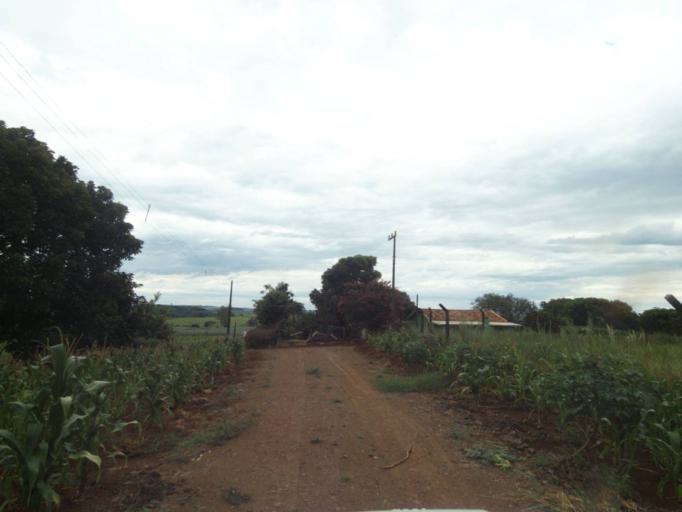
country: BR
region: Parana
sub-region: Guaraniacu
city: Guaraniacu
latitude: -24.9232
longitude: -52.9415
